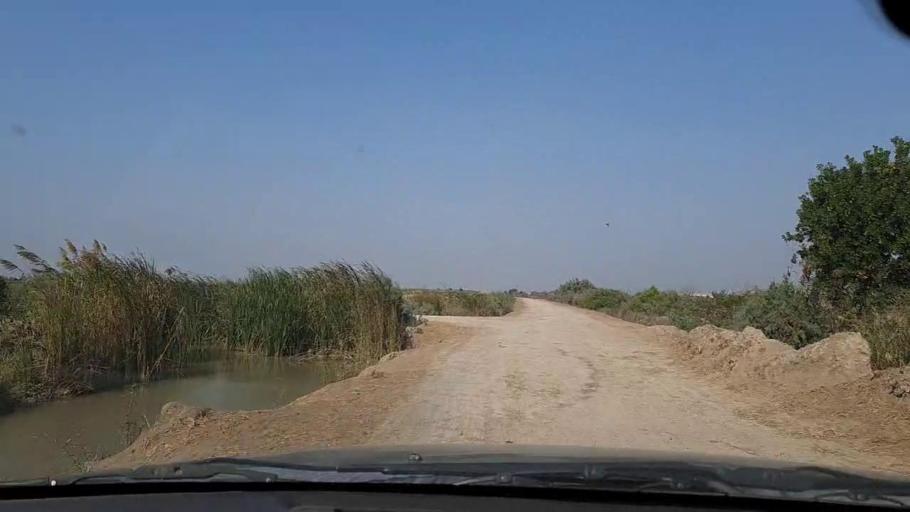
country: PK
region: Sindh
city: Mirpur Sakro
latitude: 24.3595
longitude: 67.6830
